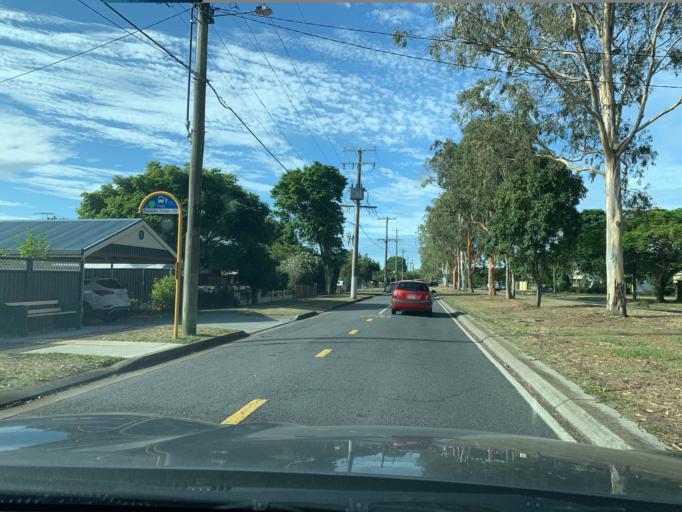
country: AU
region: Queensland
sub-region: Brisbane
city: Wynnum West
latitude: -27.4589
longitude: 153.1583
